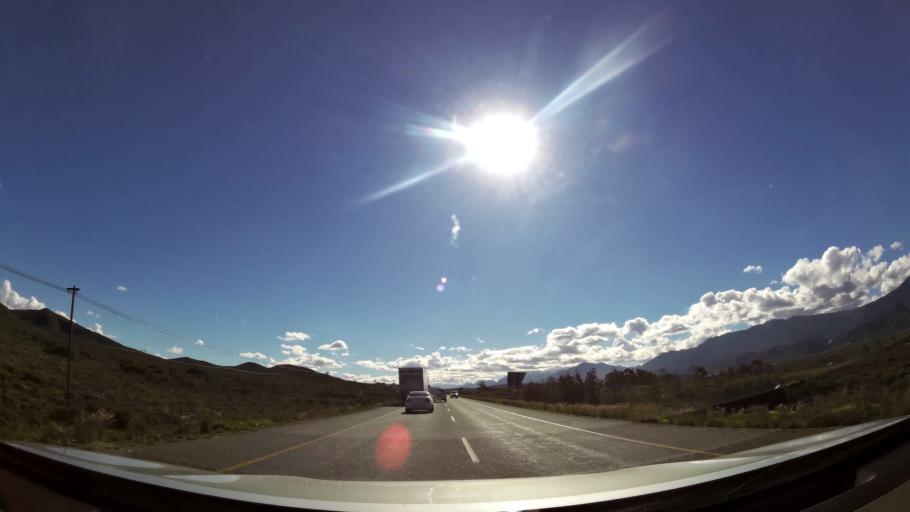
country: ZA
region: Western Cape
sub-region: Cape Winelands District Municipality
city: Ashton
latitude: -33.7658
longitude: 19.7446
